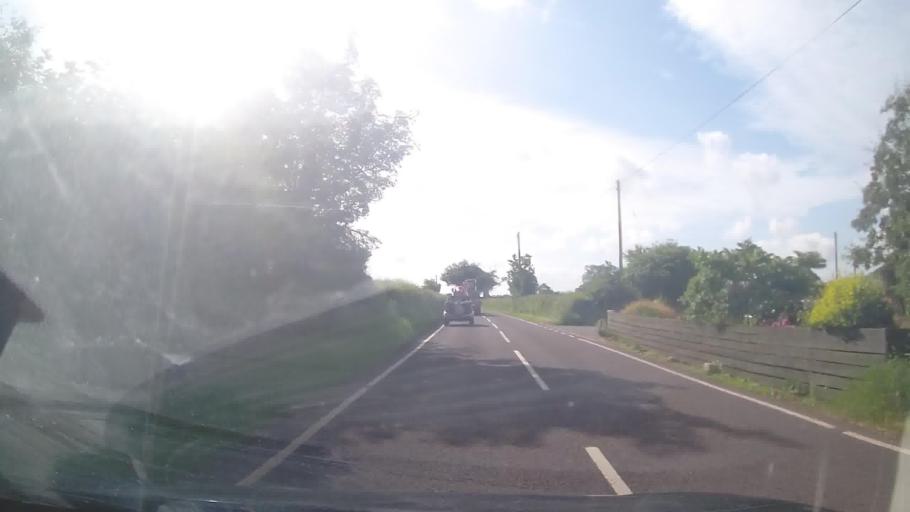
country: GB
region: England
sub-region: Shropshire
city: Wem
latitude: 52.8405
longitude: -2.7054
